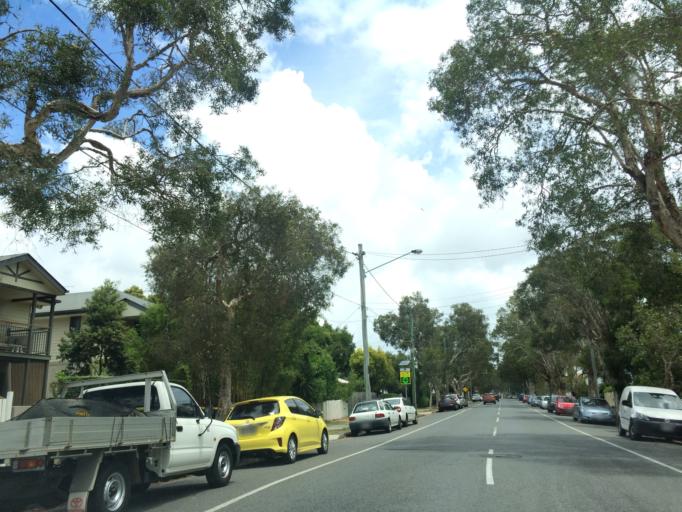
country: AU
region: Queensland
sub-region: Brisbane
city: Balmoral
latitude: -27.4556
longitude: 153.0637
